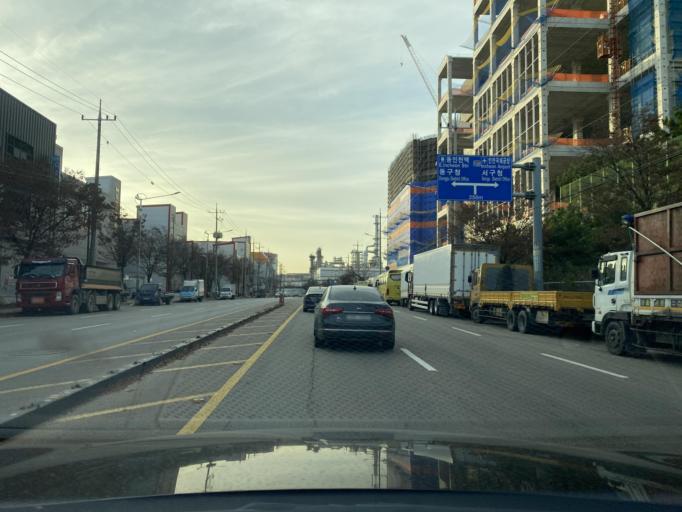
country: KR
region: Incheon
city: Incheon
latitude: 37.5067
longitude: 126.6652
